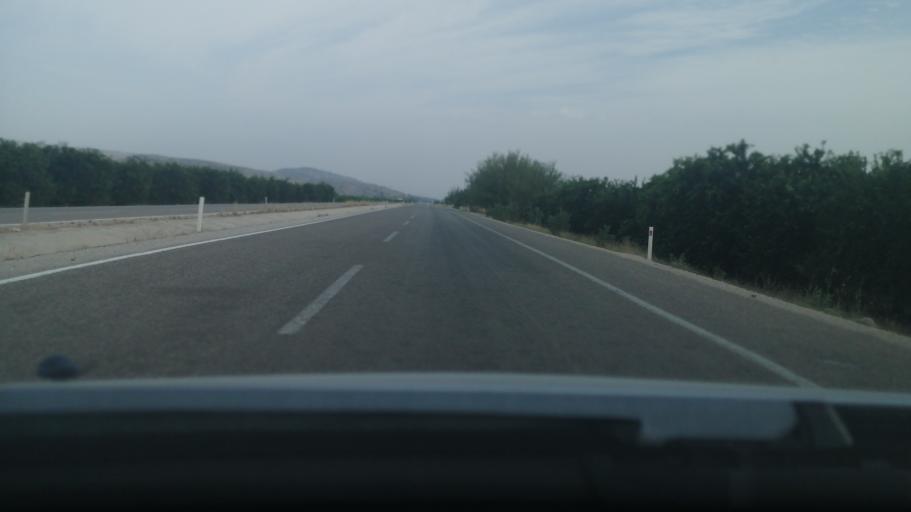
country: TR
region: Adana
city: Kozan
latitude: 37.3862
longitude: 35.8038
